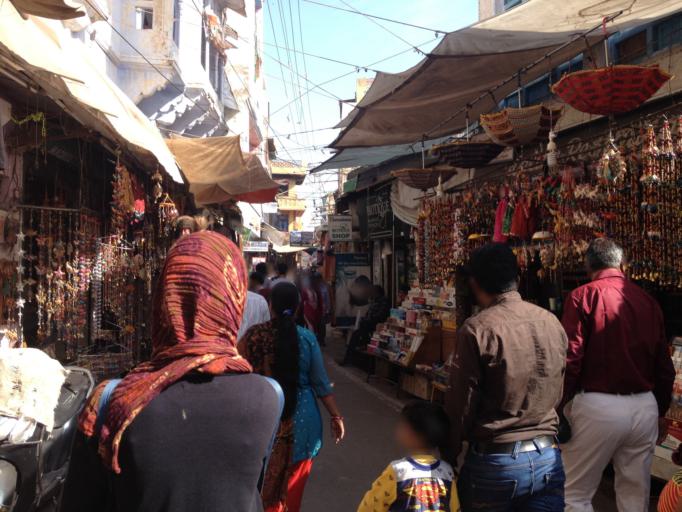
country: IN
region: Rajasthan
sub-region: Ajmer
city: Pushkar
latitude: 26.4891
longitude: 74.5523
